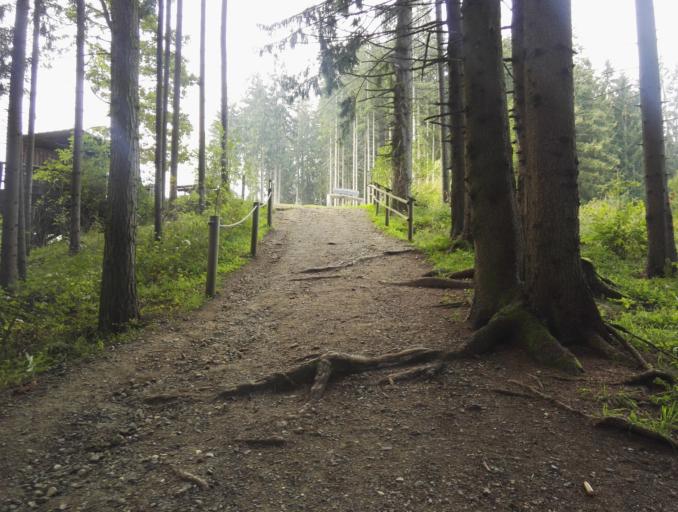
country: AT
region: Styria
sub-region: Politischer Bezirk Murtal
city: Sankt Margarethen bei Knittelfeld
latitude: 47.2162
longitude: 14.8724
